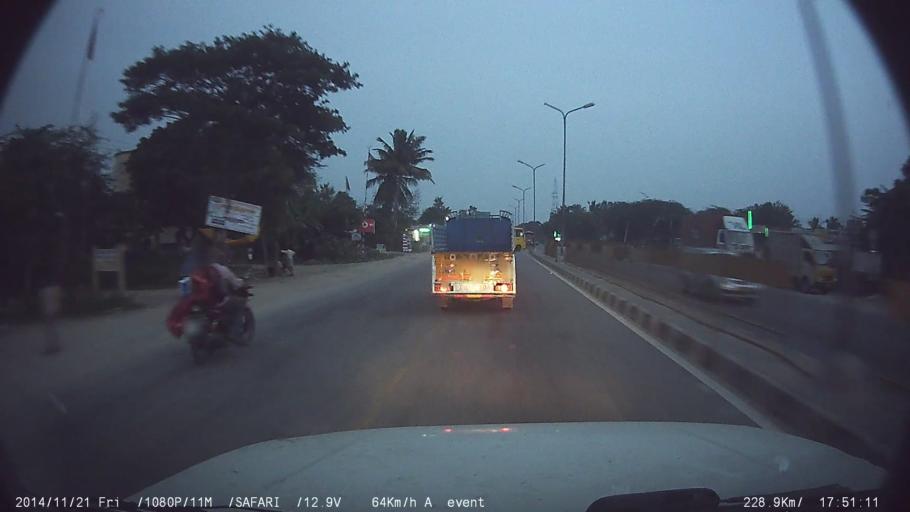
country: IN
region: Tamil Nadu
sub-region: Vellore
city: Walajapet
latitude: 12.9147
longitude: 79.3942
